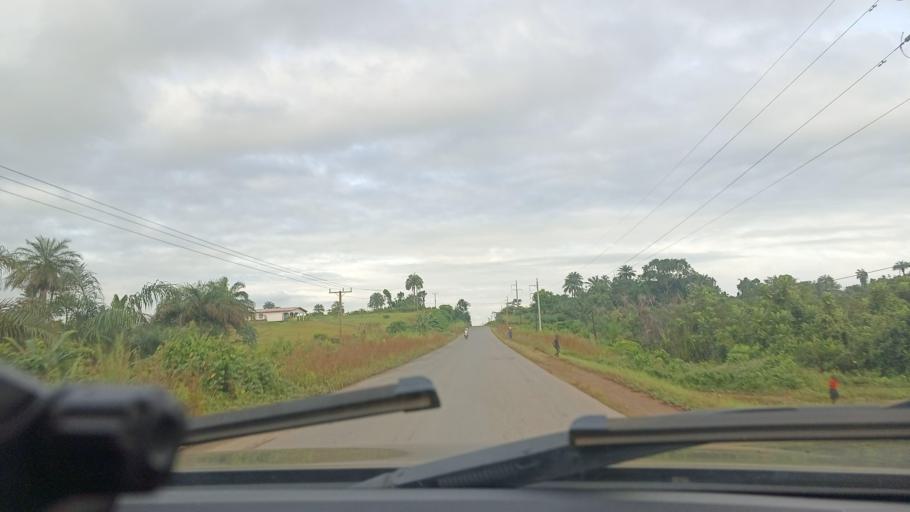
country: LR
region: Montserrado
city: Monrovia
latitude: 6.5487
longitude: -10.8621
